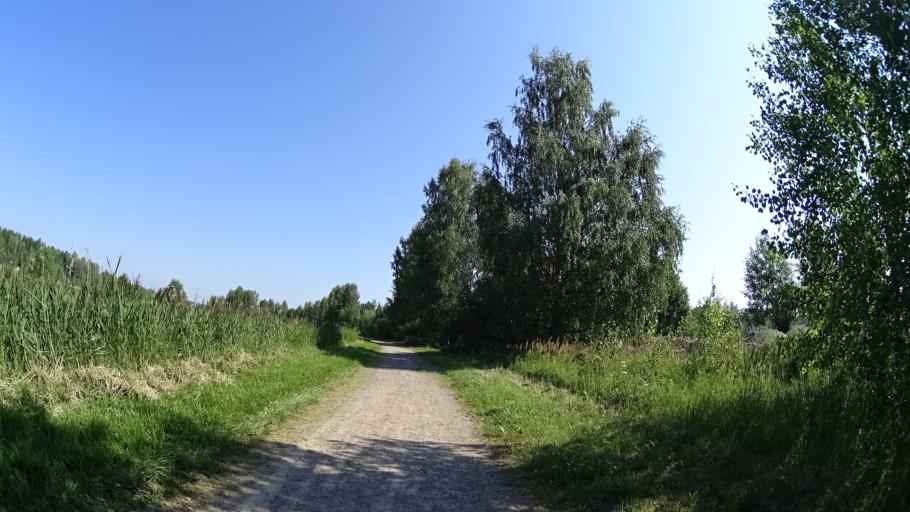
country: FI
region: Uusimaa
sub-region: Helsinki
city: Kerava
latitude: 60.3476
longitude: 25.1257
